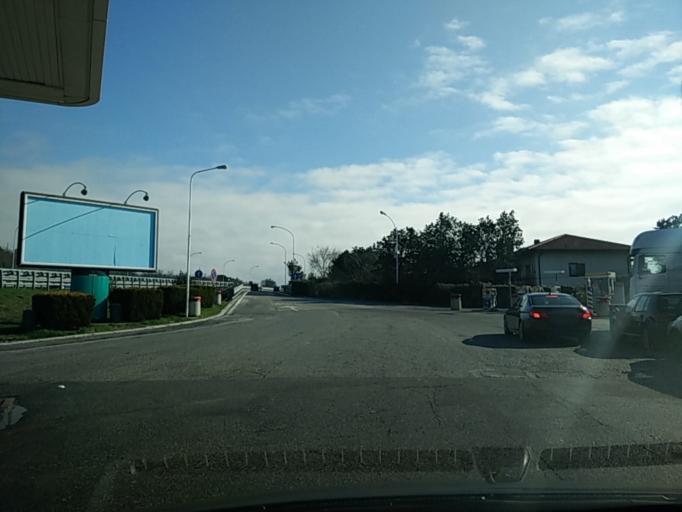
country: IT
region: Friuli Venezia Giulia
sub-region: Provincia di Trieste
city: Duino
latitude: 45.7766
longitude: 13.6085
